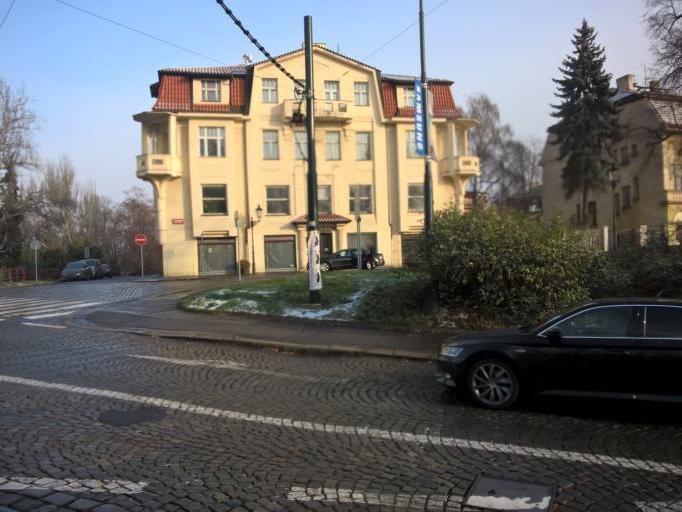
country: CZ
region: Praha
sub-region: Praha 1
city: Mala Strana
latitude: 50.0948
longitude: 14.4093
